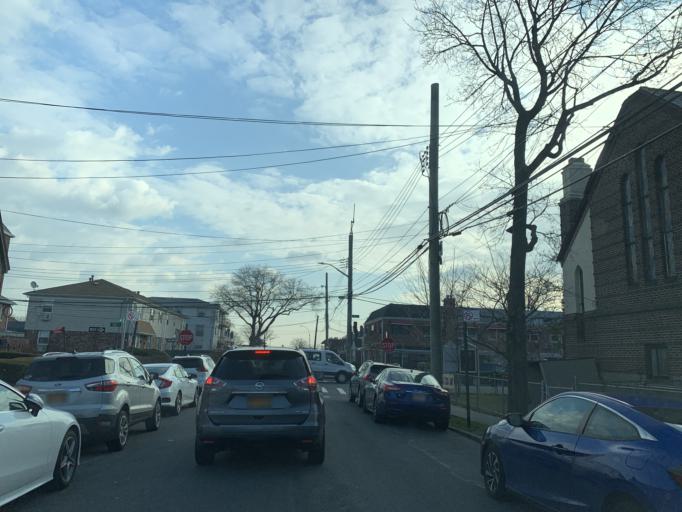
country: US
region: New York
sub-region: Queens County
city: Jamaica
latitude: 40.7435
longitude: -73.8281
